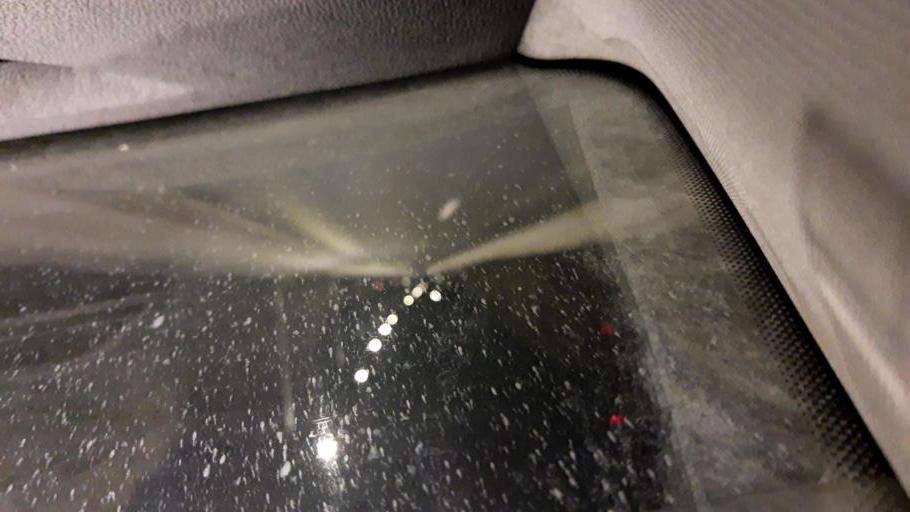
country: RU
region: Moskovskaya
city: Konstantinovo
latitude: 56.6943
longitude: 38.1334
